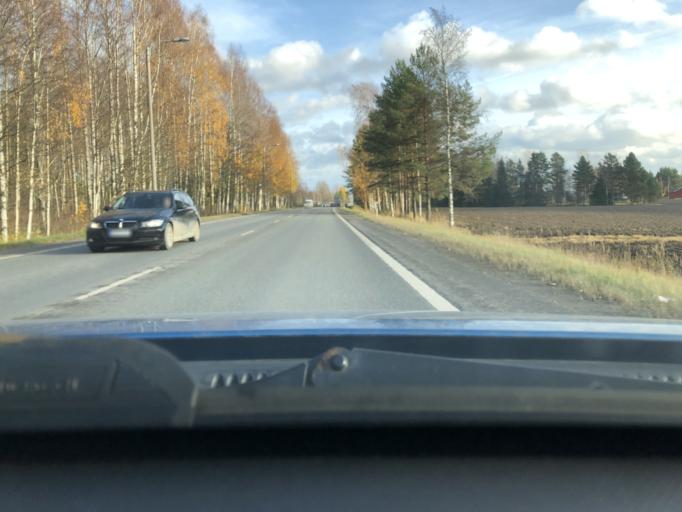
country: FI
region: Pirkanmaa
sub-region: Tampere
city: Kangasala
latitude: 61.4663
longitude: 24.0147
